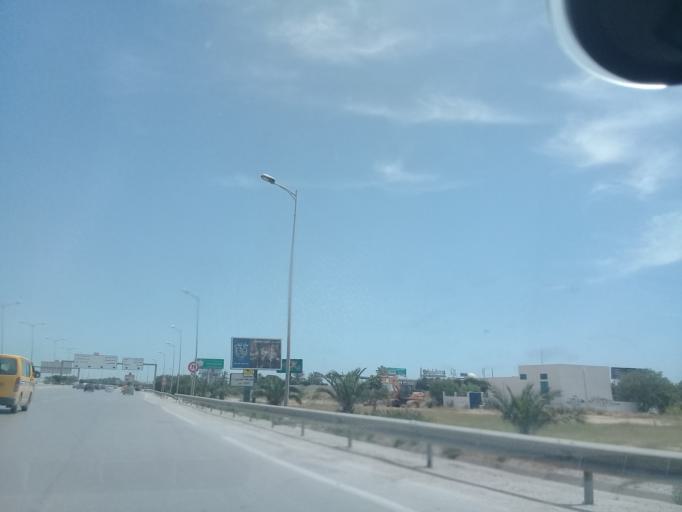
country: TN
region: Ariana
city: Ariana
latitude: 36.8322
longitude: 10.2127
